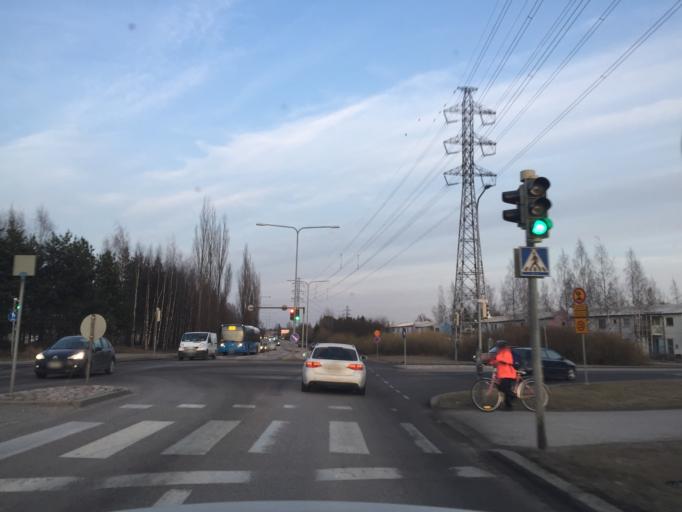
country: FI
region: Uusimaa
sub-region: Helsinki
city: Vantaa
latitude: 60.2644
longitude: 24.9829
